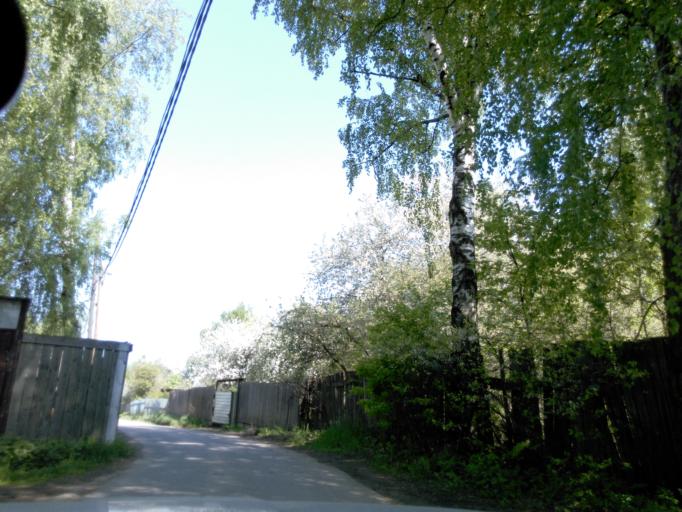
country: RU
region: Moskovskaya
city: Novopodrezkovo
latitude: 55.9482
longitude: 37.3502
